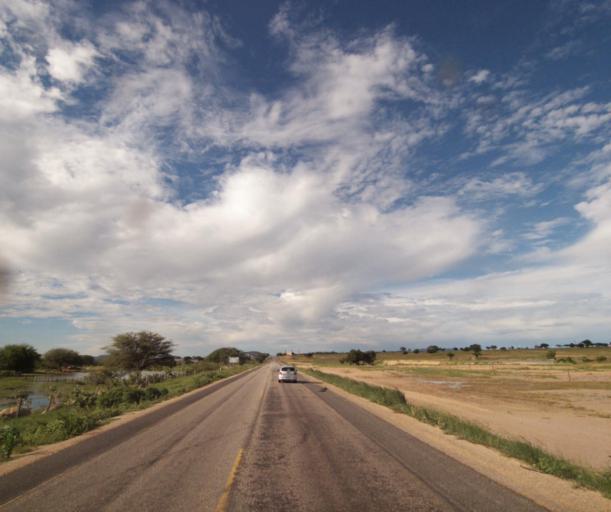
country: BR
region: Bahia
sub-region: Guanambi
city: Guanambi
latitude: -14.2746
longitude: -42.7833
